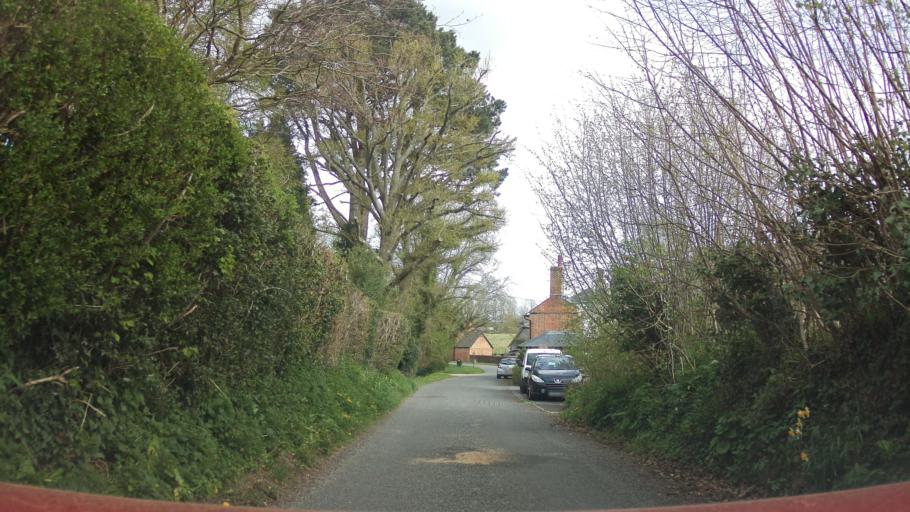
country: GB
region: England
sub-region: Hampshire
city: Romsey
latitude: 51.0233
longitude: -1.4715
